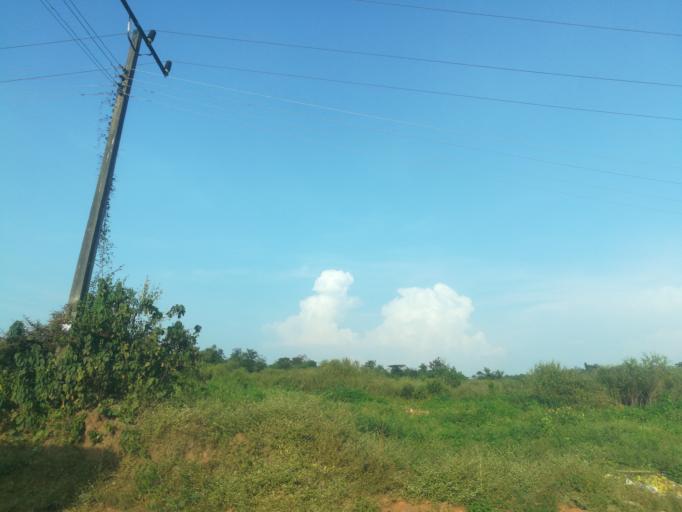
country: NG
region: Oyo
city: Moniya
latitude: 7.5512
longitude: 3.8911
